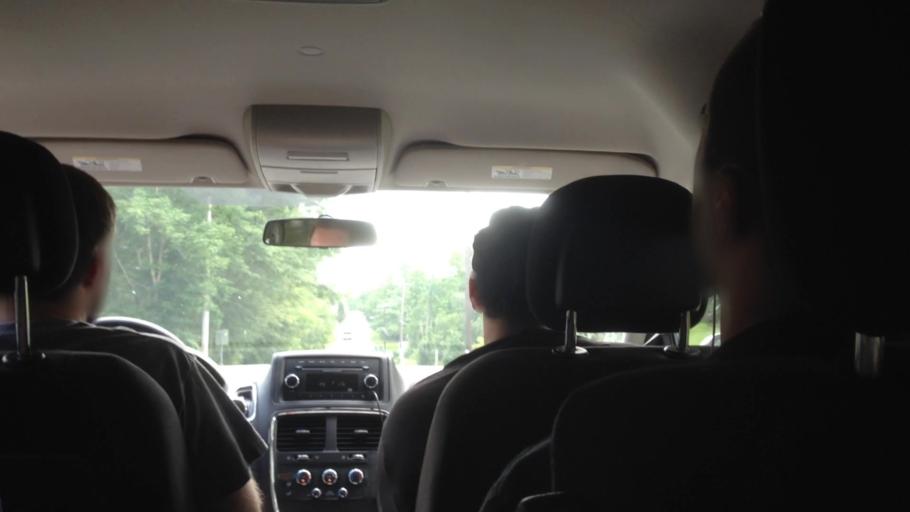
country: US
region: New York
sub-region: Dutchess County
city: Tivoli
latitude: 42.0551
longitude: -73.8983
